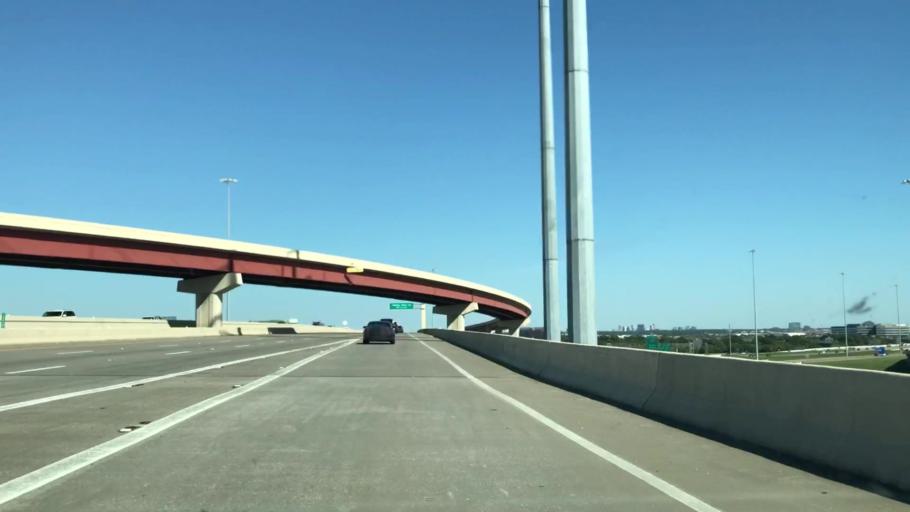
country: US
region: Texas
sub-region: Dallas County
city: Farmers Branch
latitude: 32.9111
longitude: -96.9451
